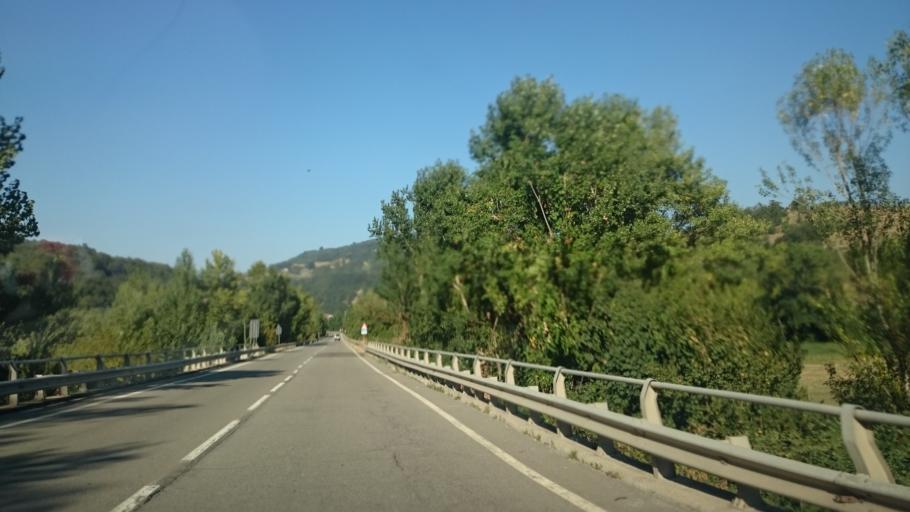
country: IT
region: Emilia-Romagna
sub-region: Provincia di Modena
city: Prignano
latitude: 44.4270
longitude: 10.6403
